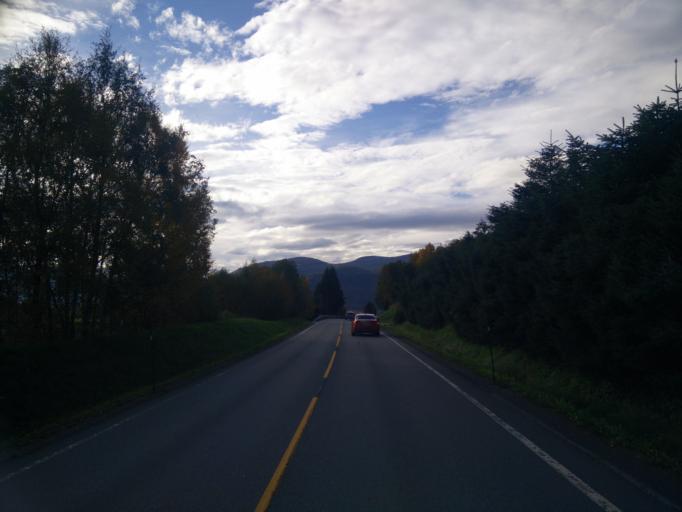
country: NO
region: More og Romsdal
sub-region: Vestnes
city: Vestnes
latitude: 62.6377
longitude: 7.0767
